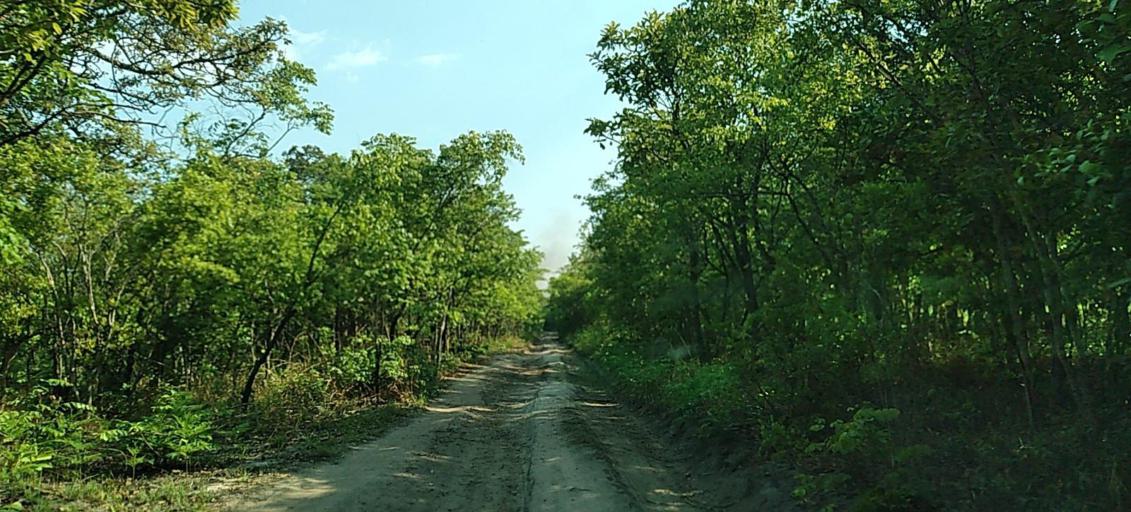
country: ZM
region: North-Western
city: Mwinilunga
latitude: -11.3202
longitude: 24.7392
